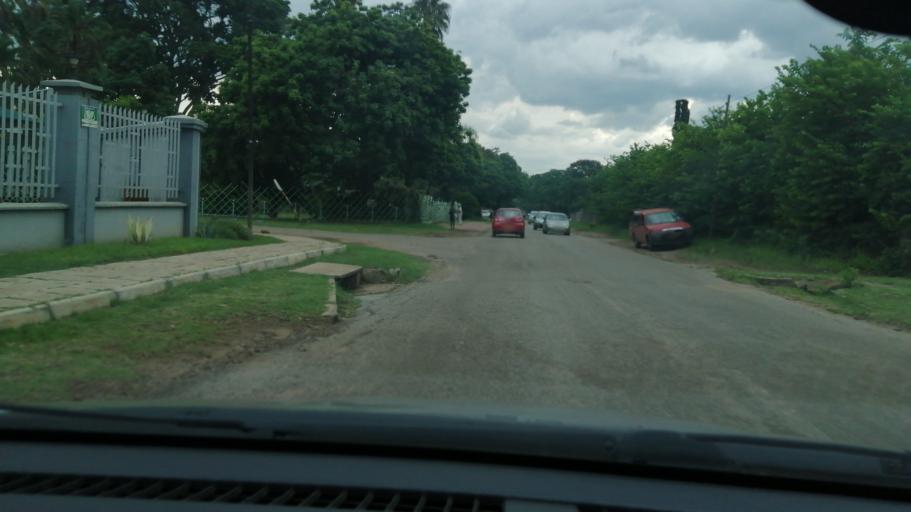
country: ZW
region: Harare
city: Harare
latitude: -17.7992
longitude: 31.0416
